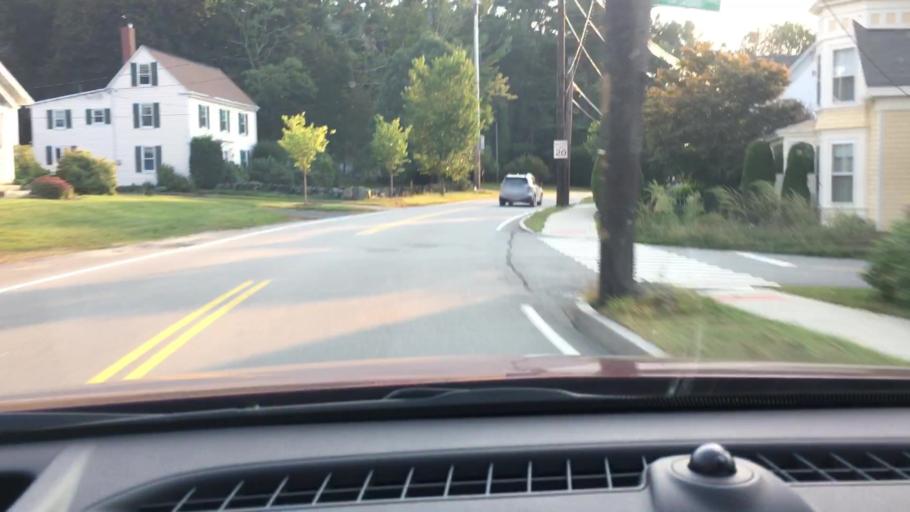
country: US
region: New Hampshire
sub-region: Rockingham County
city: Portsmouth
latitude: 43.0632
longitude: -70.7633
